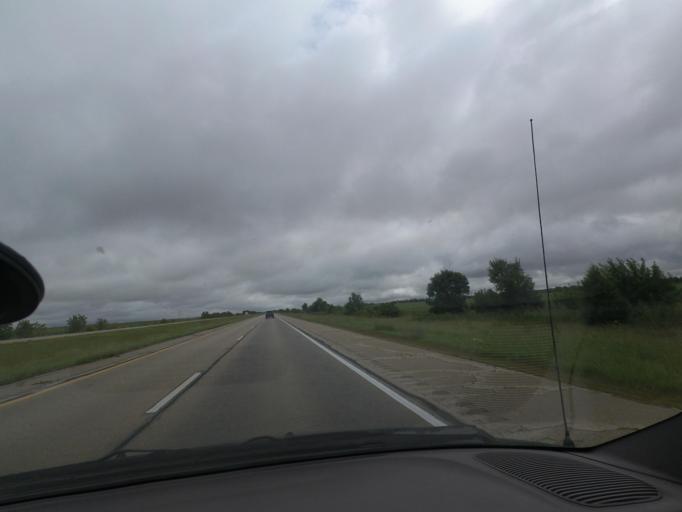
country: US
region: Illinois
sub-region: Piatt County
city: Monticello
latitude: 40.0243
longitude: -88.6830
